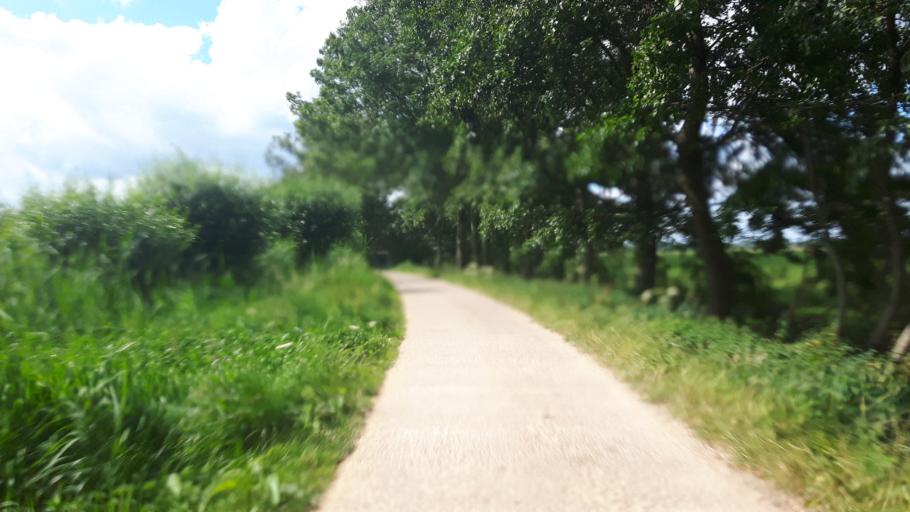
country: NL
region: South Holland
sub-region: Gemeente Vlist
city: Vlist
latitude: 51.9910
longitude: 4.7983
